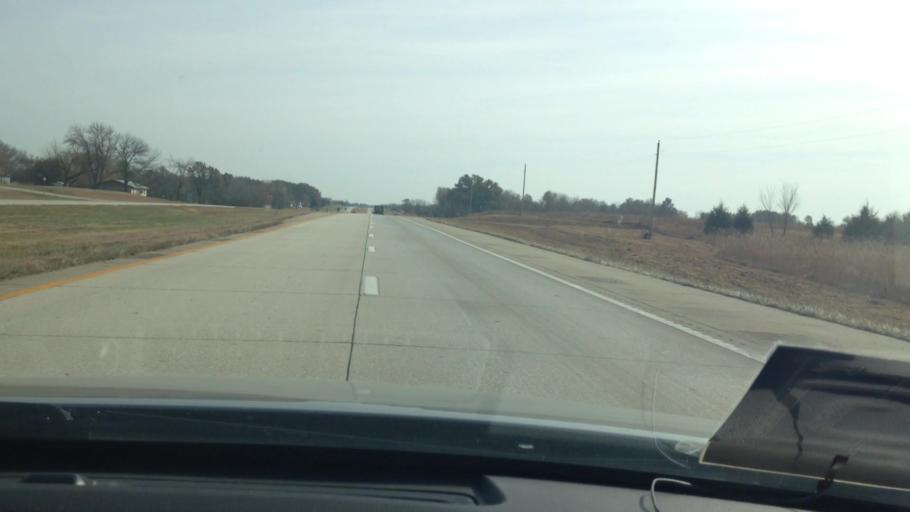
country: US
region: Missouri
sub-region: Henry County
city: Clinton
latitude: 38.4209
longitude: -93.8717
